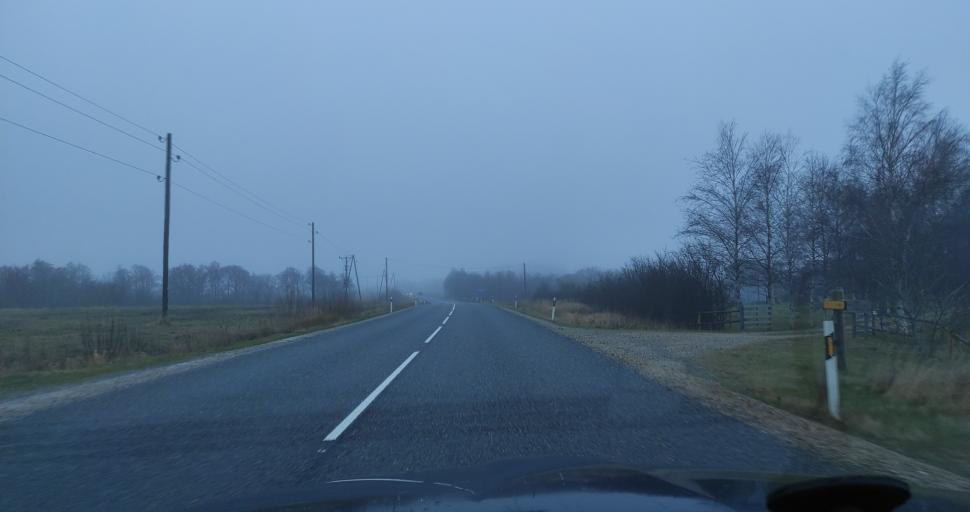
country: LV
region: Alsunga
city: Alsunga
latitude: 56.9896
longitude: 21.3632
